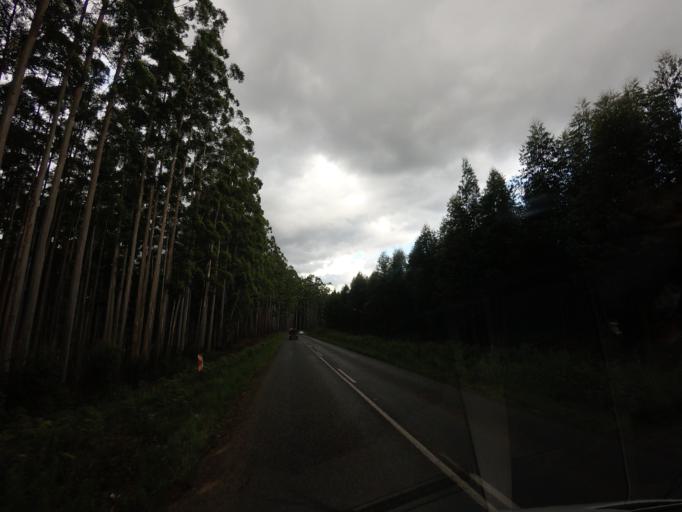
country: ZA
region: Mpumalanga
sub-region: Ehlanzeni District
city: Graksop
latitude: -24.9563
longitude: 30.8991
